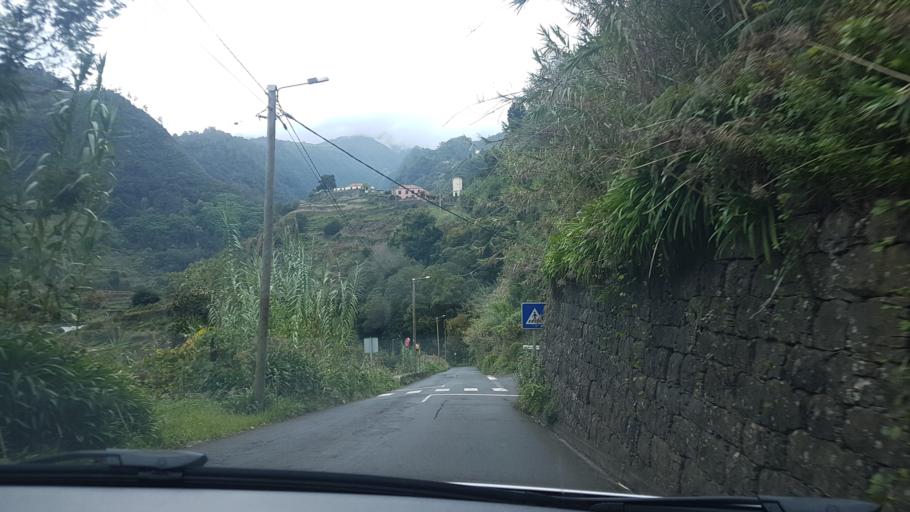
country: PT
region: Madeira
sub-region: Santana
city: Santana
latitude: 32.8212
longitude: -16.9002
